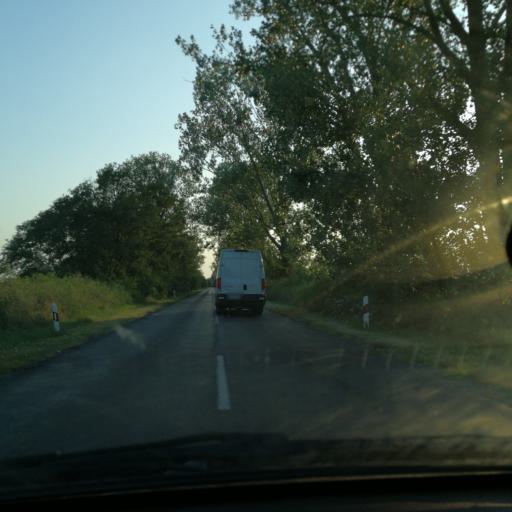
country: HU
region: Bacs-Kiskun
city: Kiskunhalas
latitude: 46.4354
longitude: 19.5434
